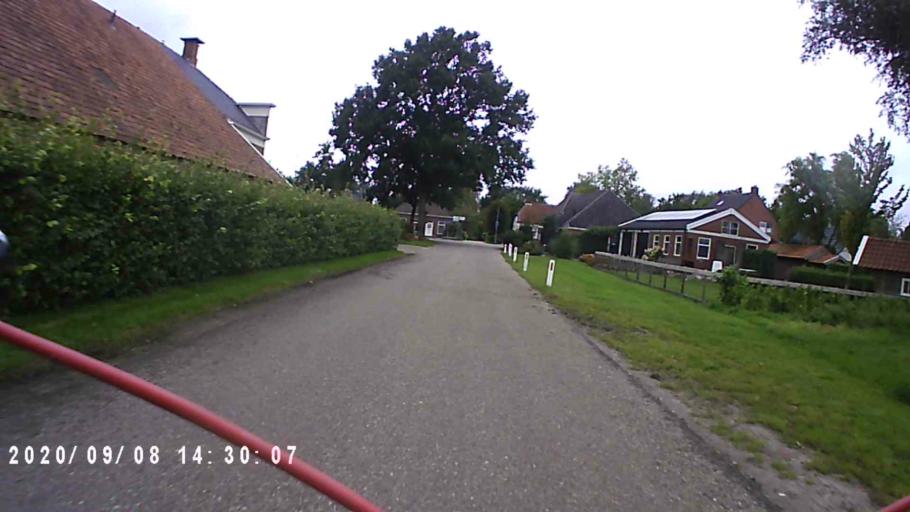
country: NL
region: Groningen
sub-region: Gemeente Slochteren
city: Slochteren
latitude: 53.2263
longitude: 6.8117
